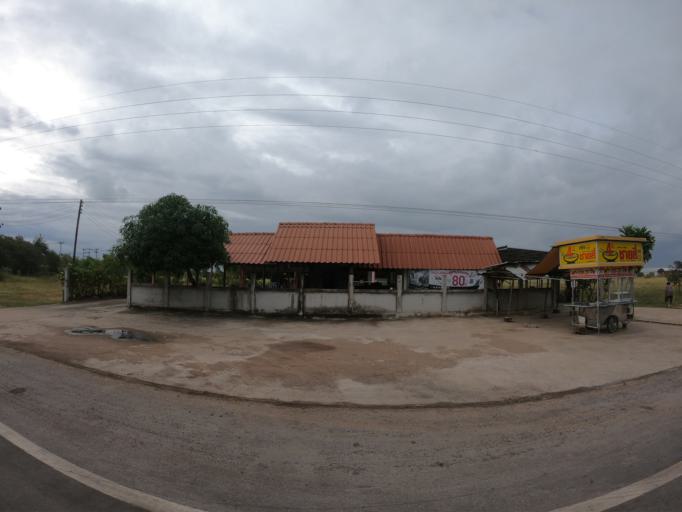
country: TH
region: Roi Et
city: Thawat Buri
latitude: 16.0821
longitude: 103.7098
